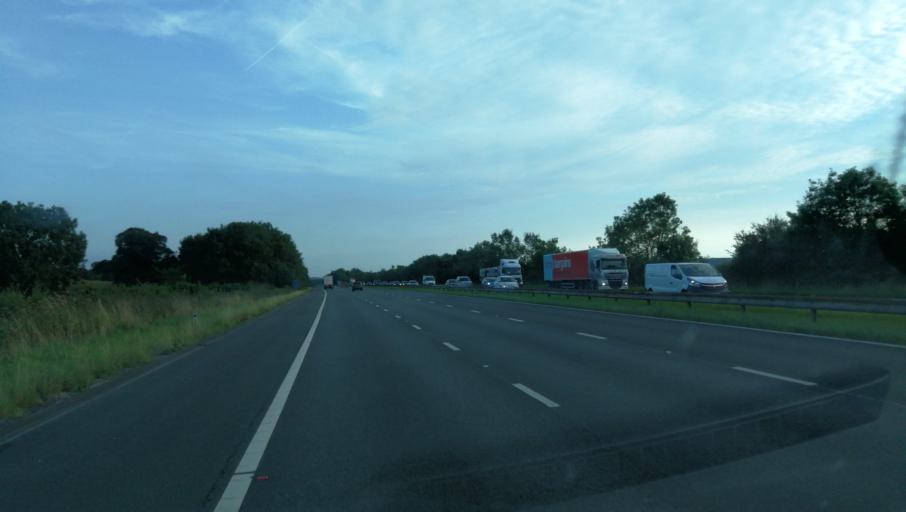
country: GB
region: England
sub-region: Cumbria
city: Milnthorpe
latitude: 54.2061
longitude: -2.7238
